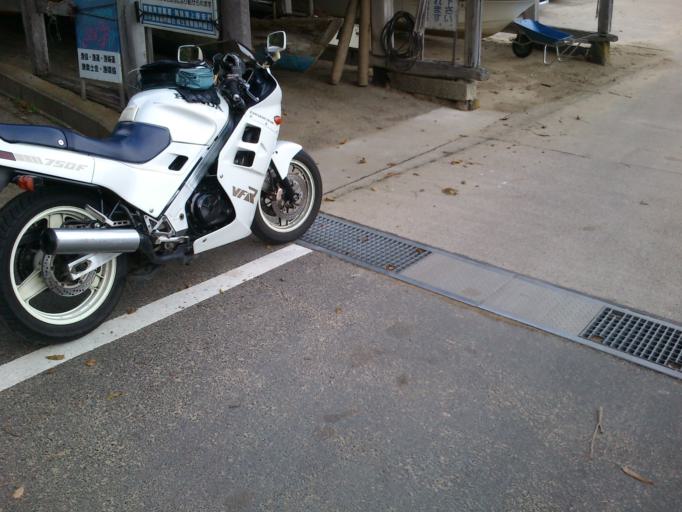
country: JP
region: Kyoto
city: Maizuru
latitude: 35.5782
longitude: 135.4477
